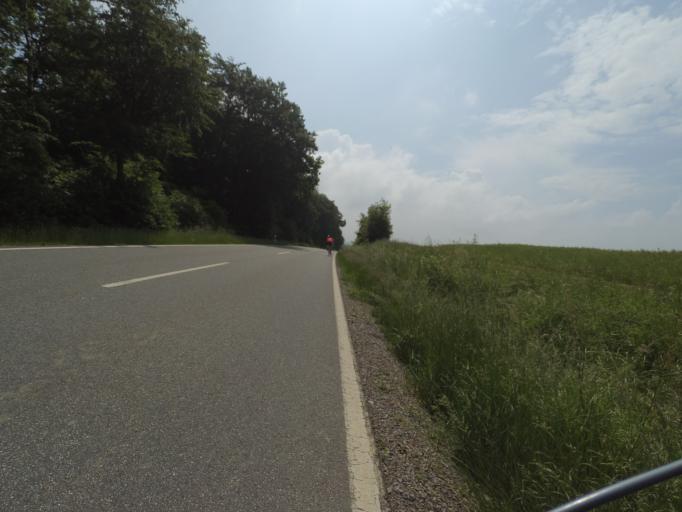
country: DE
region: Rheinland-Pfalz
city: Mittelstrimmig
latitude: 50.0820
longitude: 7.2842
